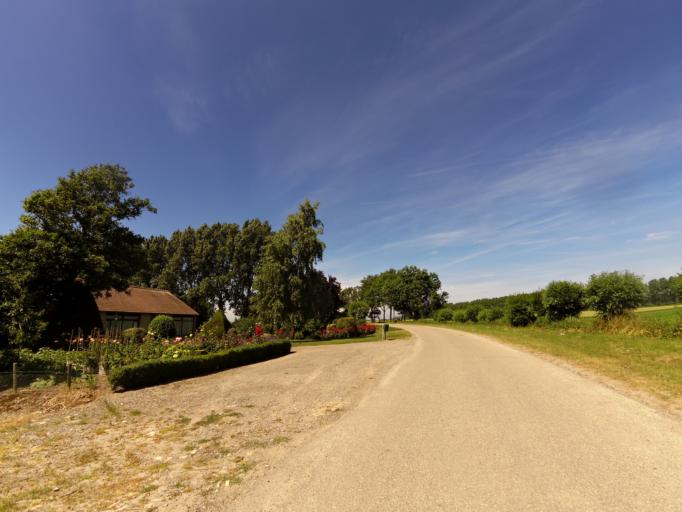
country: NL
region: Zeeland
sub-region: Gemeente Sluis
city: Sluis
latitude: 51.3198
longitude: 3.3756
